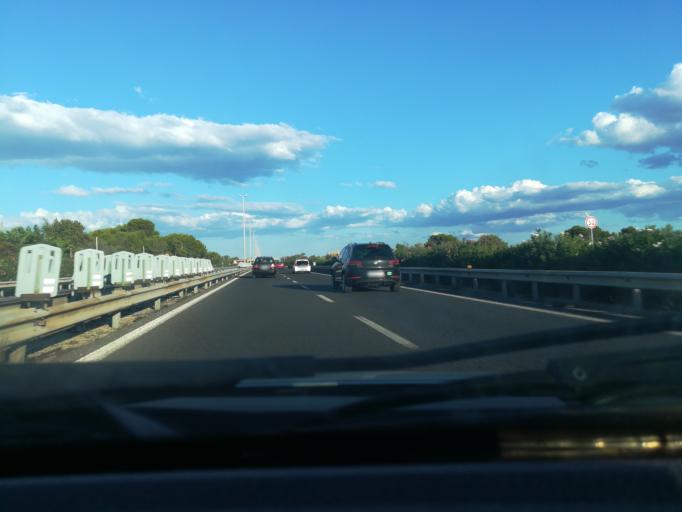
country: IT
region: Apulia
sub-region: Provincia di Bari
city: Parco Scizzo-Parchitello
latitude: 41.0790
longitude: 17.0387
